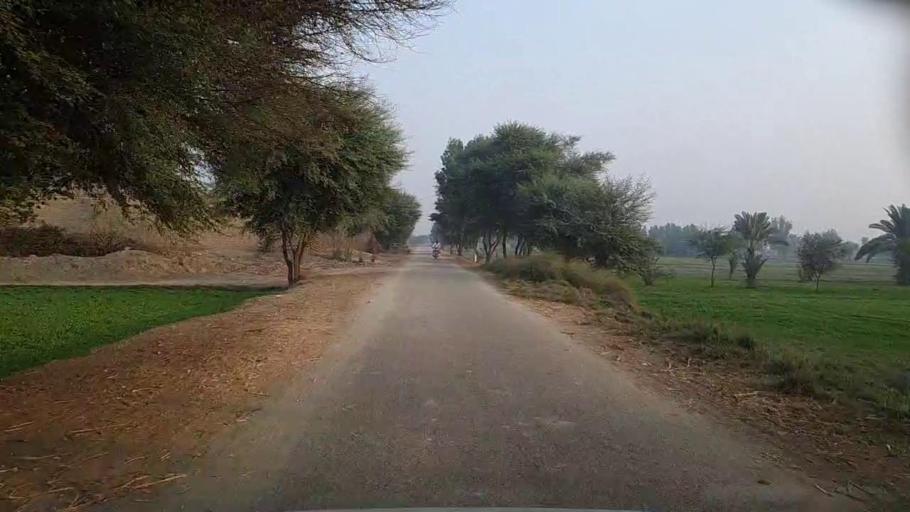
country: PK
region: Sindh
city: Bozdar
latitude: 27.0773
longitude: 68.5817
